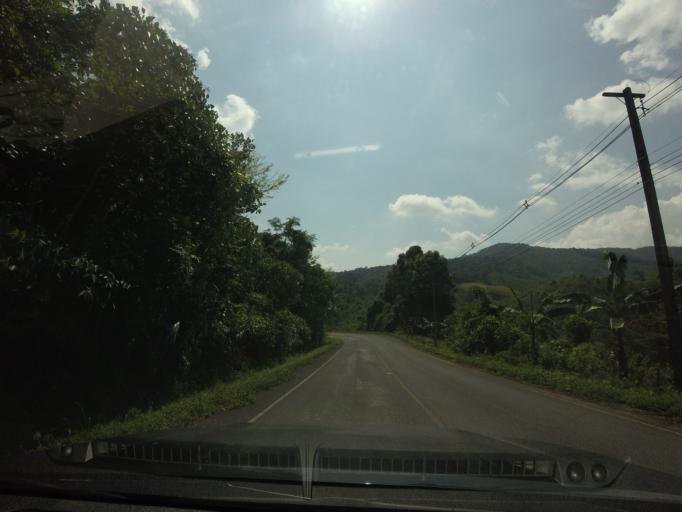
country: TH
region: Nan
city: Bo Kluea
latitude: 19.0640
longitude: 101.0998
